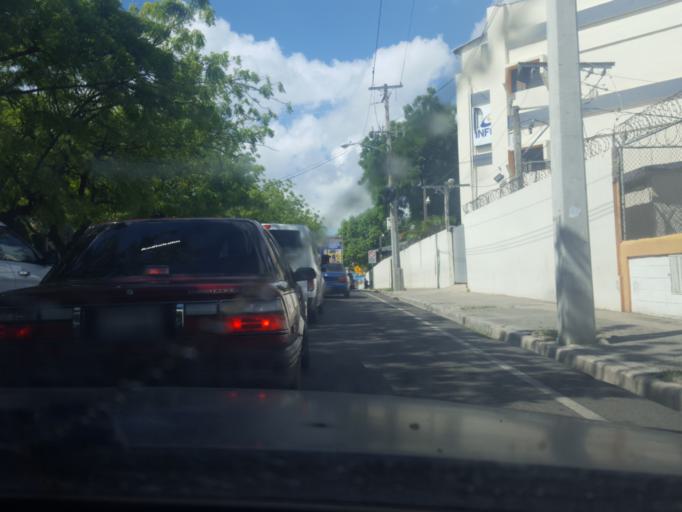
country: DO
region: Santiago
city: Santiago de los Caballeros
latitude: 19.4825
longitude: -70.7050
